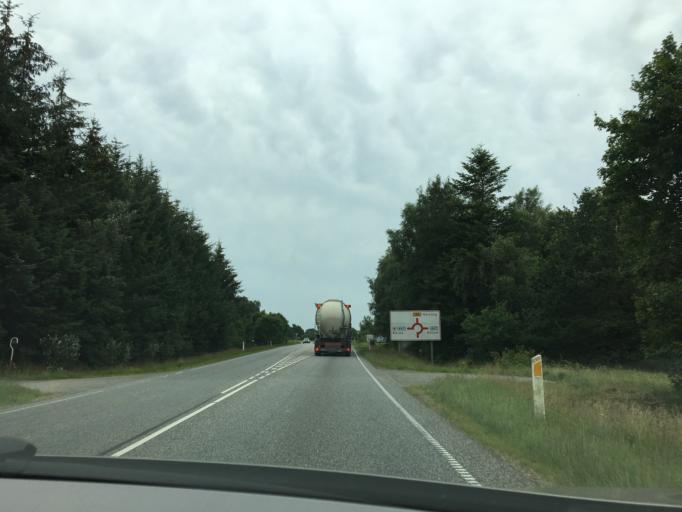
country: DK
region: Central Jutland
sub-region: Herning Kommune
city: Sunds
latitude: 56.3338
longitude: 8.9838
